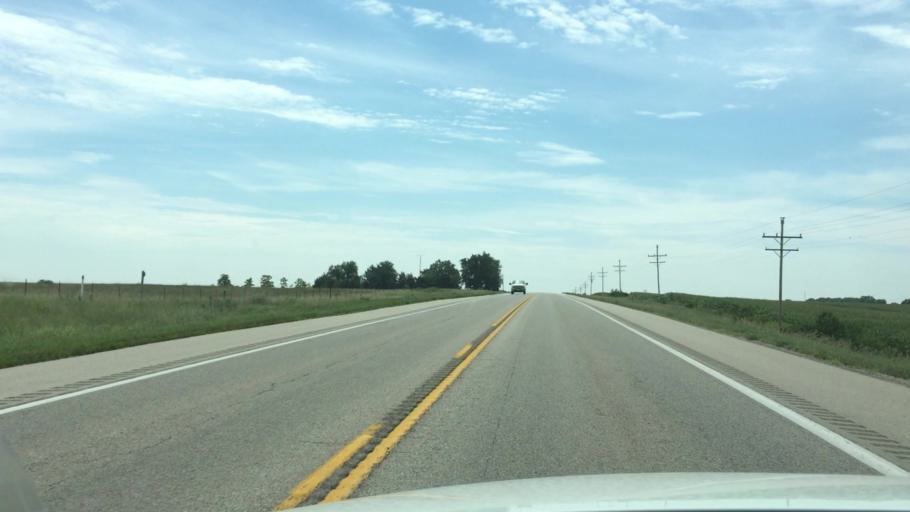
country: US
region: Kansas
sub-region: Nemaha County
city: Sabetha
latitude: 39.7890
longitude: -95.7295
